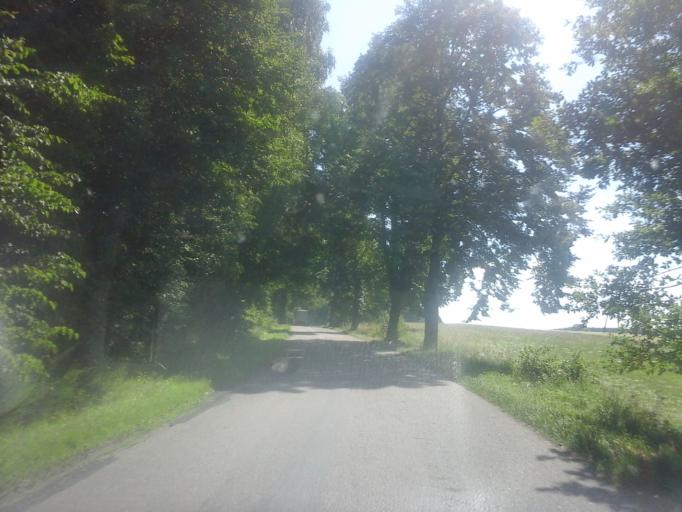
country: PL
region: West Pomeranian Voivodeship
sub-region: Powiat bialogardzki
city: Tychowo
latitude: 54.0303
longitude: 16.1640
